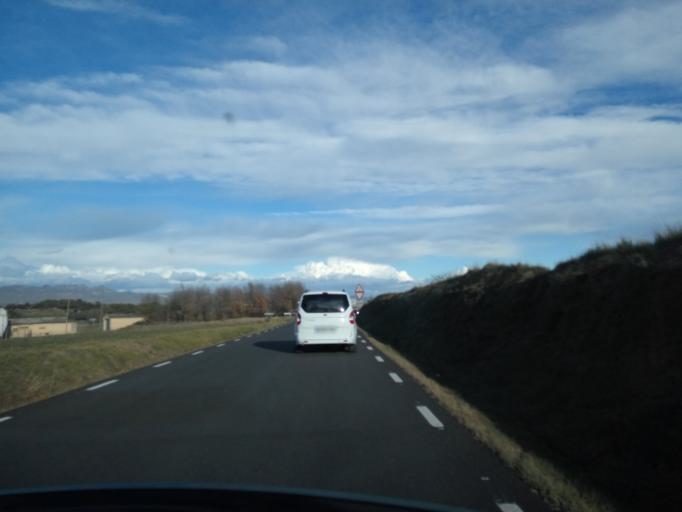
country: ES
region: Catalonia
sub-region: Provincia de Barcelona
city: Gironella
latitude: 42.0126
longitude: 1.8275
